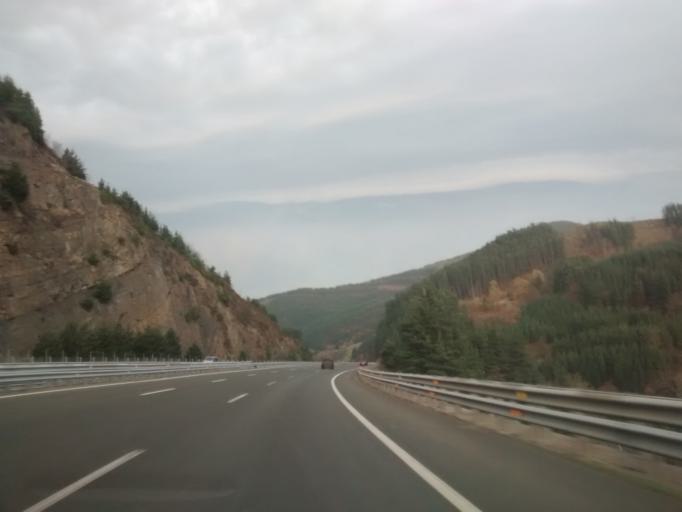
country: ES
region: Basque Country
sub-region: Provincia de Alava
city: Lezama
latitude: 43.0712
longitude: -2.9238
